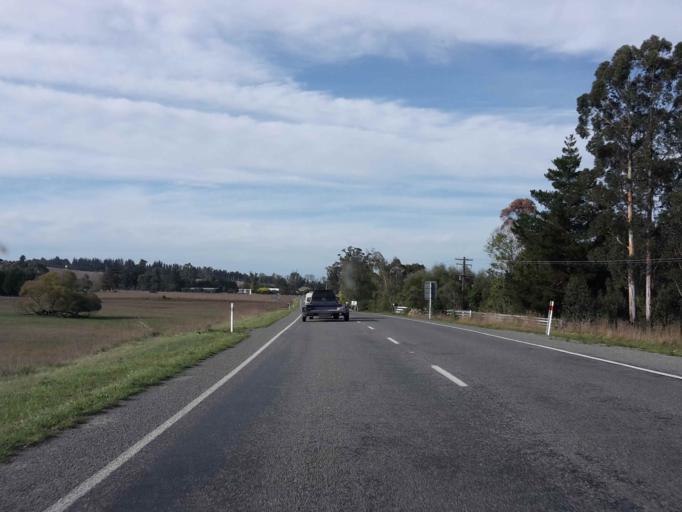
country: NZ
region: Canterbury
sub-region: Timaru District
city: Pleasant Point
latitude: -44.1160
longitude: 171.2108
